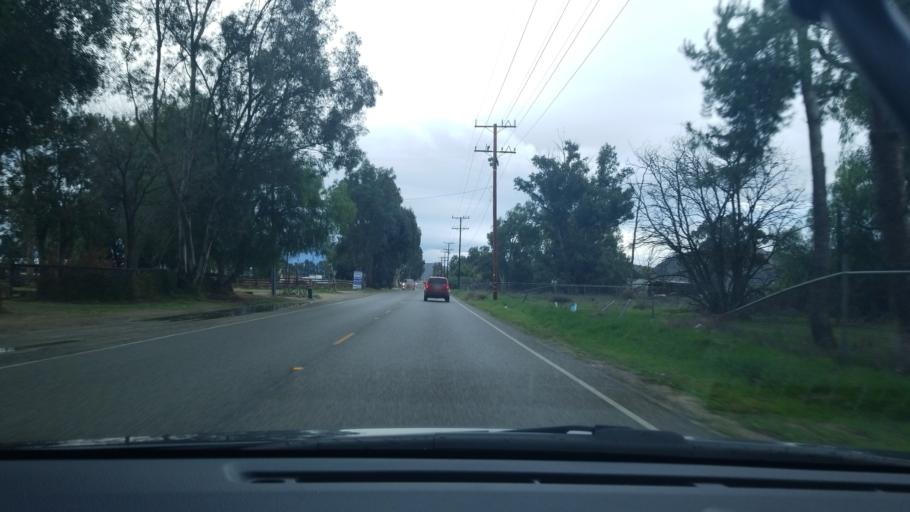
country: US
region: California
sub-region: Riverside County
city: Winchester
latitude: 33.7074
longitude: -117.0577
